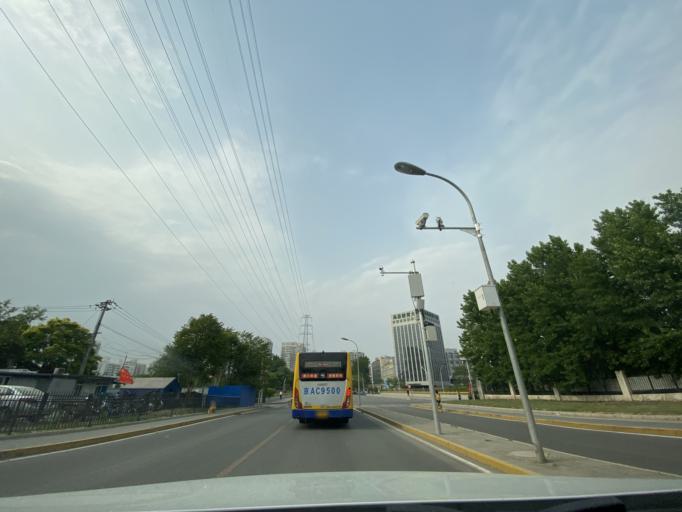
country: CN
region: Beijing
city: Qinghe
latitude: 39.9843
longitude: 116.3345
